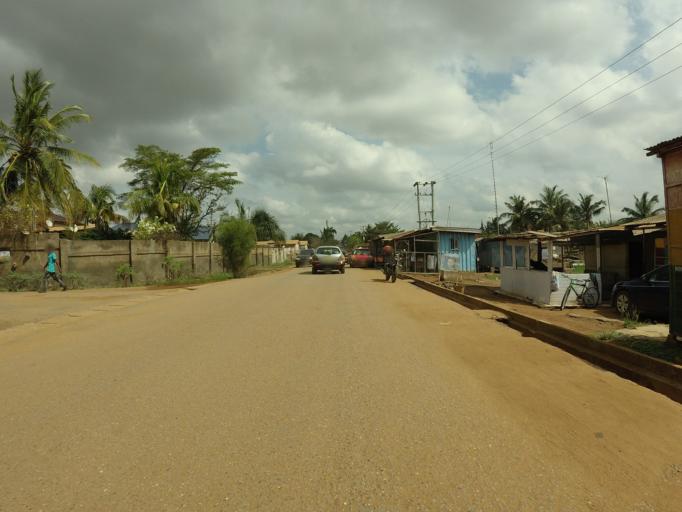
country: GH
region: Greater Accra
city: Nungua
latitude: 5.6137
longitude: -0.1010
